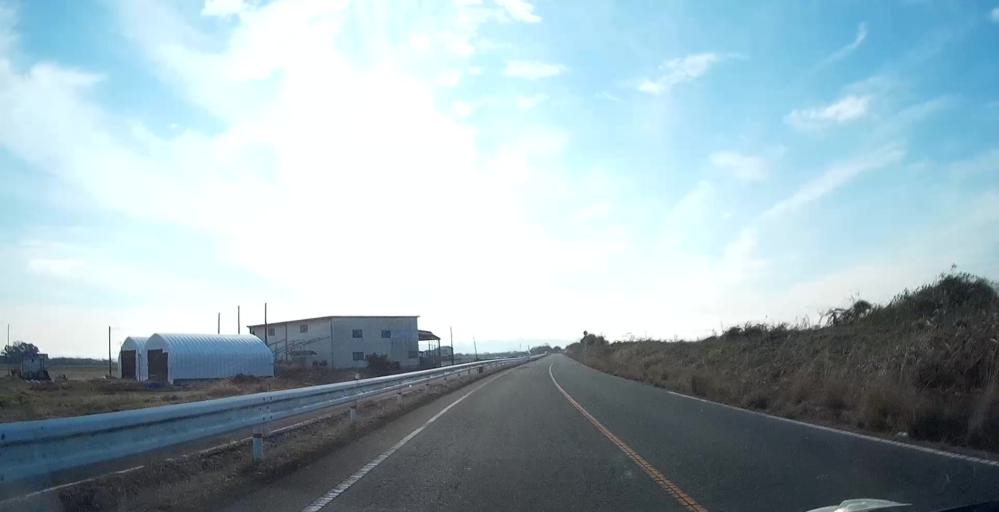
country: JP
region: Kumamoto
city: Uto
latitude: 32.7413
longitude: 130.6705
